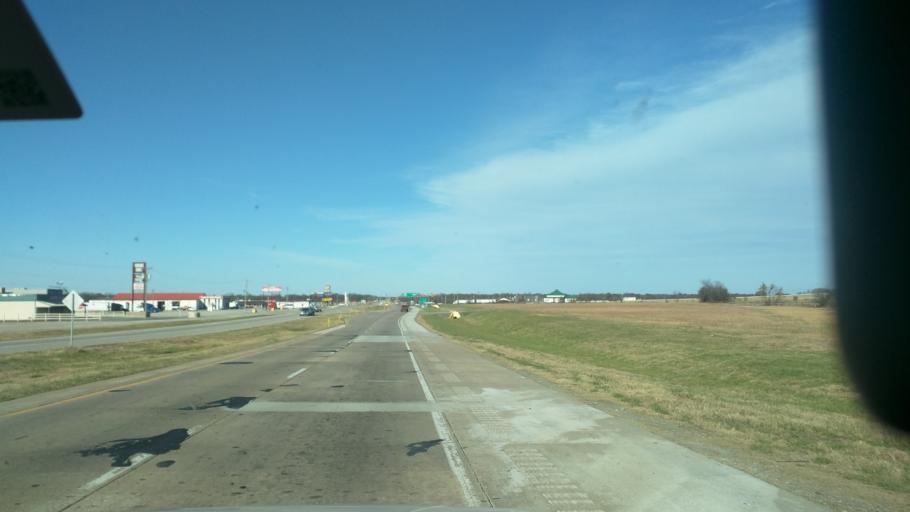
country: US
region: Oklahoma
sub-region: Craig County
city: Vinita
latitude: 36.5606
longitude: -95.2201
